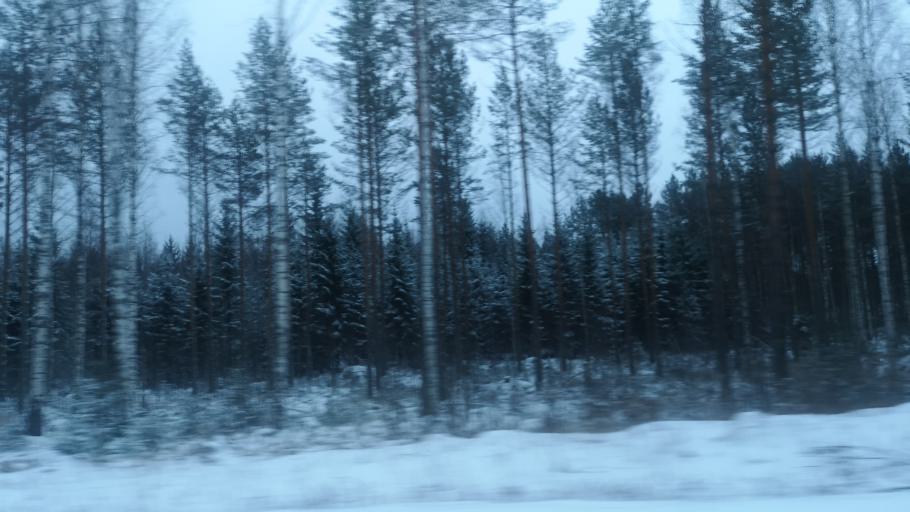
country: FI
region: Southern Savonia
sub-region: Savonlinna
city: Enonkoski
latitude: 62.0933
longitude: 28.6707
